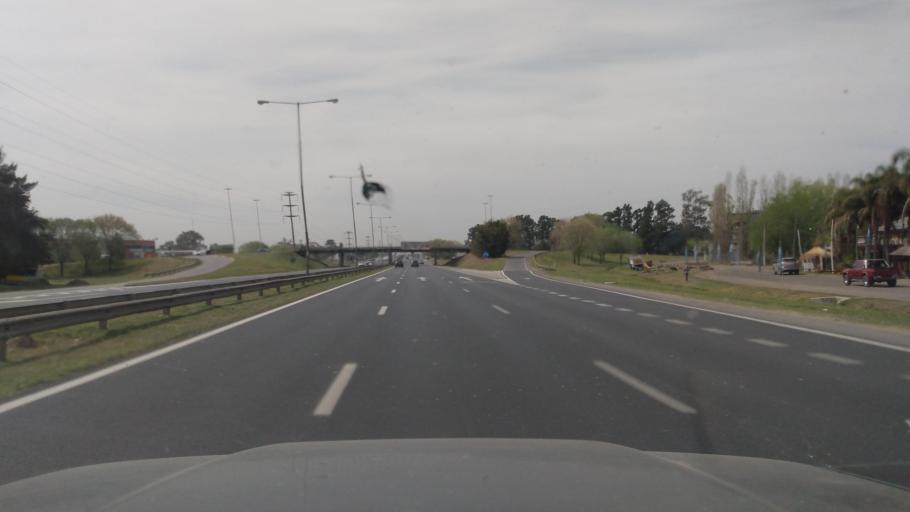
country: AR
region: Buenos Aires
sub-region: Partido de Pilar
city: Pilar
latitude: -34.4531
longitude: -58.9323
